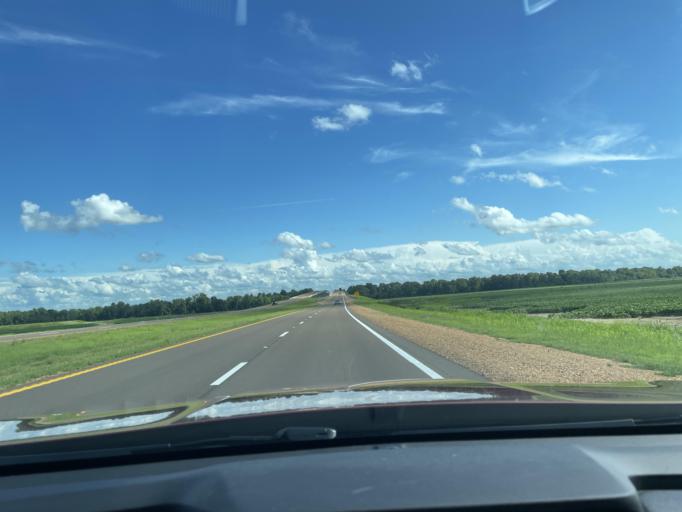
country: US
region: Mississippi
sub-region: Yazoo County
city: Yazoo City
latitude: 32.9362
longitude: -90.4132
